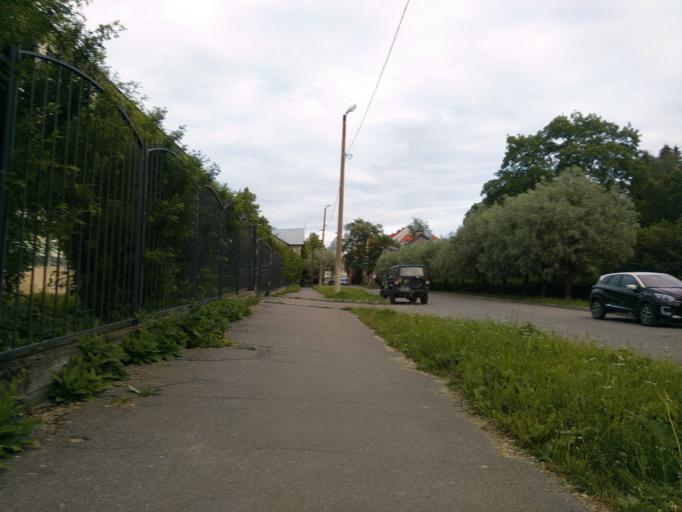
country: RU
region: Republic of Karelia
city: Sortavala
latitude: 61.7040
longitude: 30.6869
